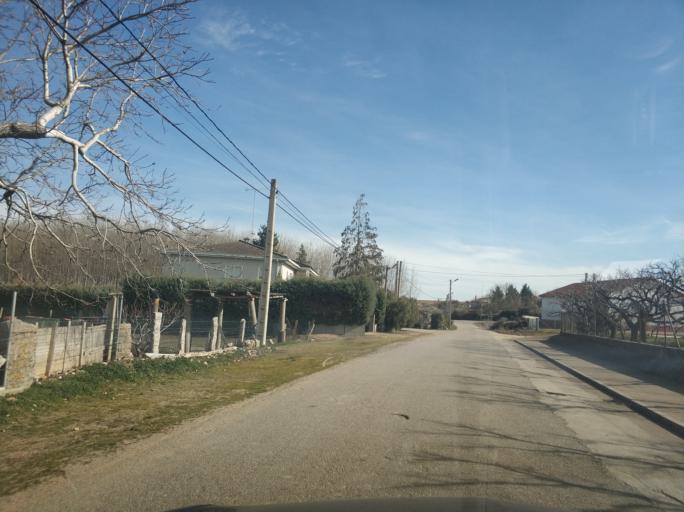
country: ES
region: Castille and Leon
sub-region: Provincia de Salamanca
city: Valverdon
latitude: 41.0394
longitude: -5.7897
